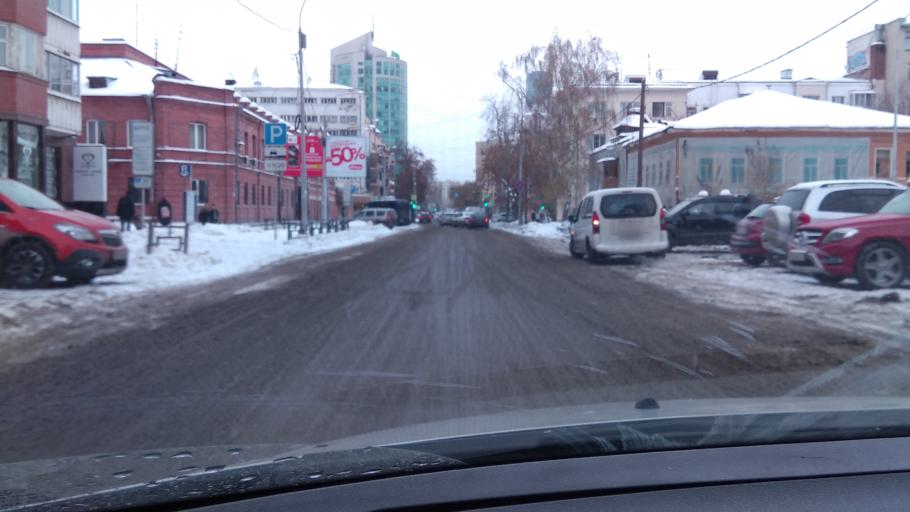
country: RU
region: Sverdlovsk
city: Yekaterinburg
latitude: 56.8320
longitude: 60.5929
